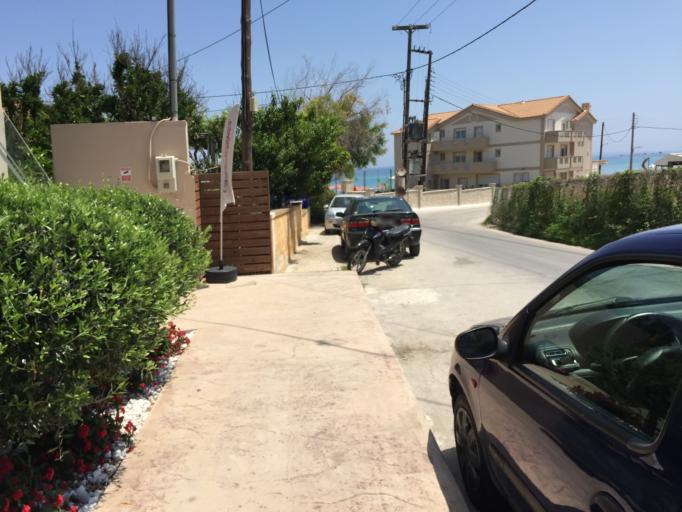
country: GR
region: Ionian Islands
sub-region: Nomos Zakynthou
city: Vanaton
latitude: 37.8180
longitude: 20.8663
